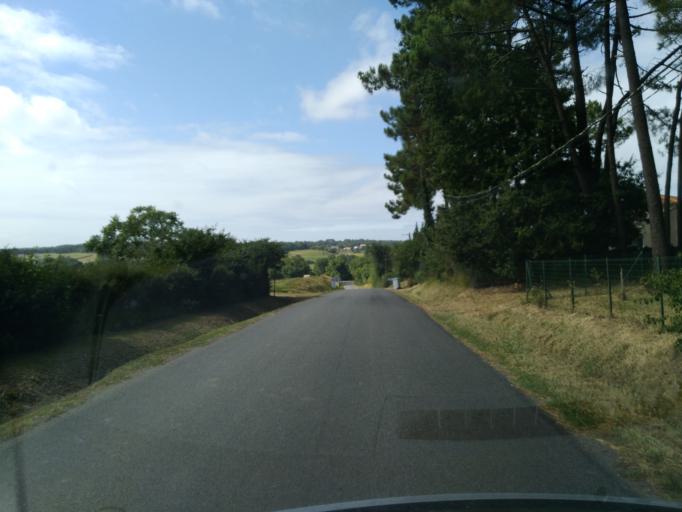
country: FR
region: Poitou-Charentes
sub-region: Departement de la Charente-Maritime
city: Breuillet
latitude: 45.6856
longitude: -1.0775
